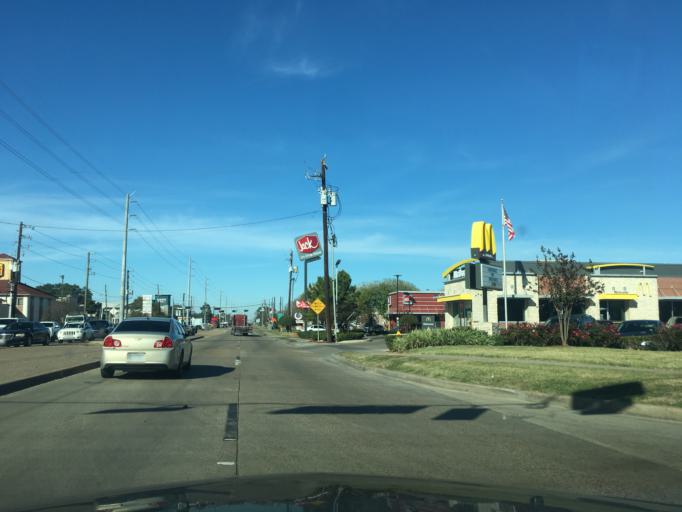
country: US
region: Texas
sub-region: Fort Bend County
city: Rosenberg
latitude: 29.5326
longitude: -95.8082
